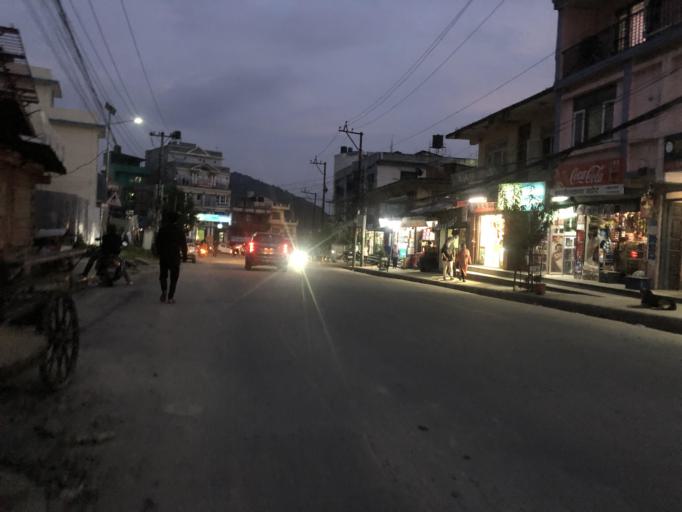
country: NP
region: Central Region
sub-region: Bagmati Zone
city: Kathmandu
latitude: 27.7774
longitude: 85.3616
